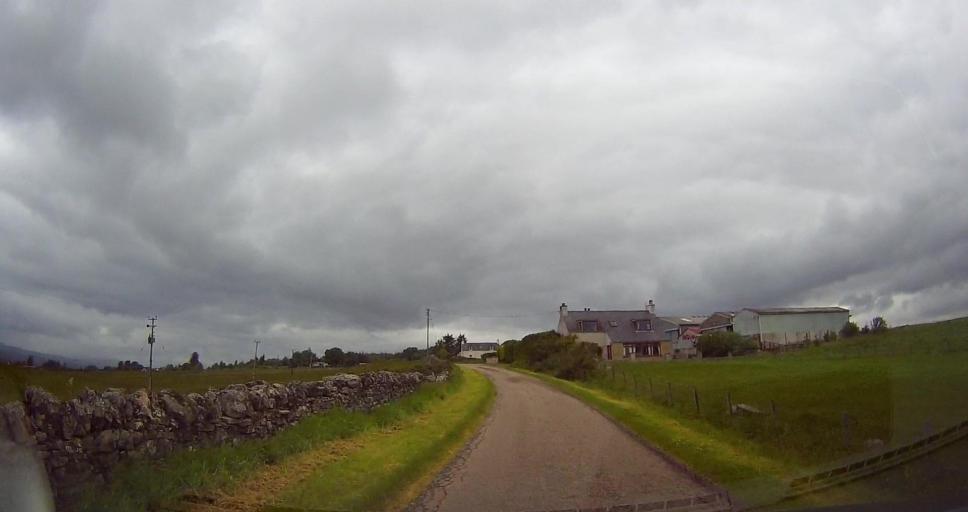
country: GB
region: Scotland
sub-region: Highland
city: Alness
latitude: 58.0776
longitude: -4.4444
